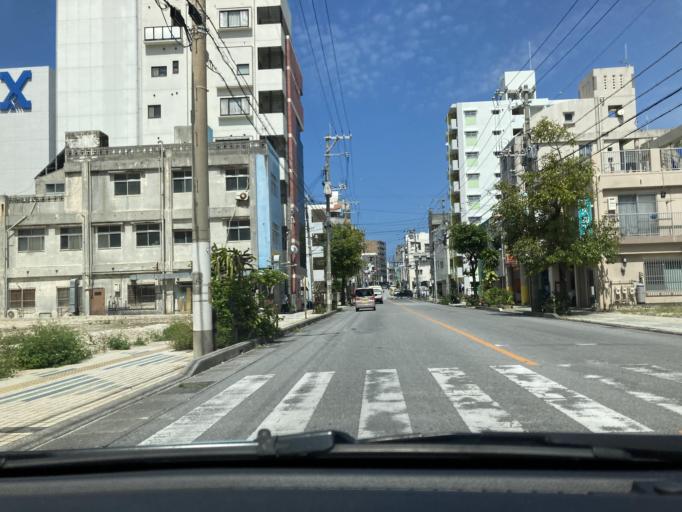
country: JP
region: Okinawa
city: Naha-shi
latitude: 26.2138
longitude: 127.6709
